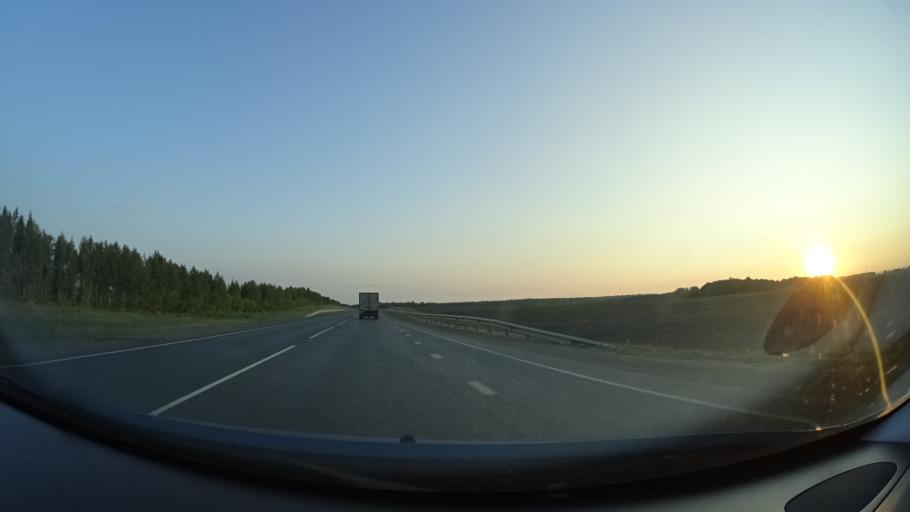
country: RU
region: Samara
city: Sernovodsk
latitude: 53.9304
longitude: 51.3286
